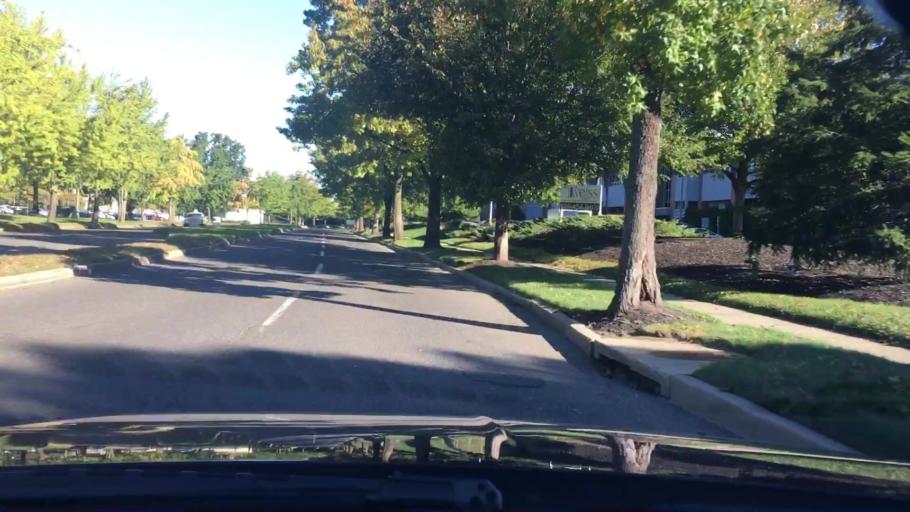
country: US
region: New York
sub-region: Suffolk County
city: Melville
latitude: 40.7717
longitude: -73.4134
